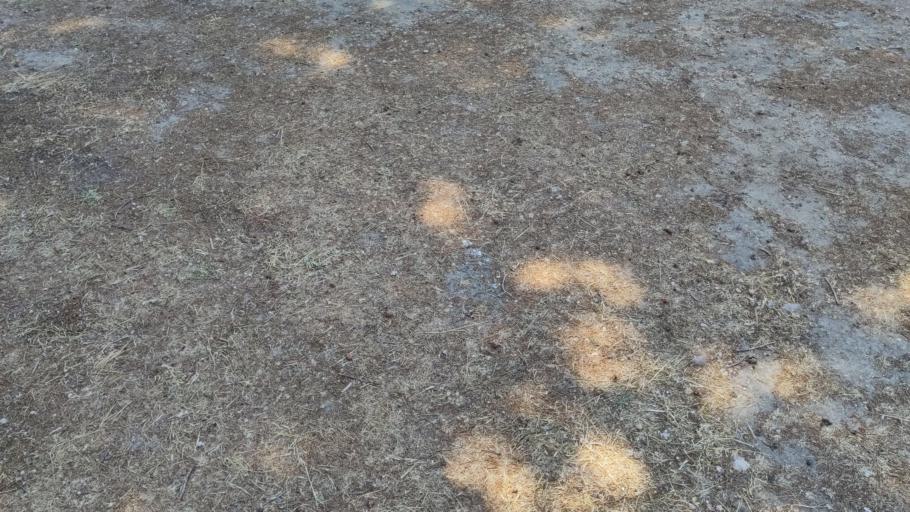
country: GR
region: South Aegean
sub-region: Nomos Dodekanisou
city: Trianta
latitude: 36.3987
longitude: 28.1446
